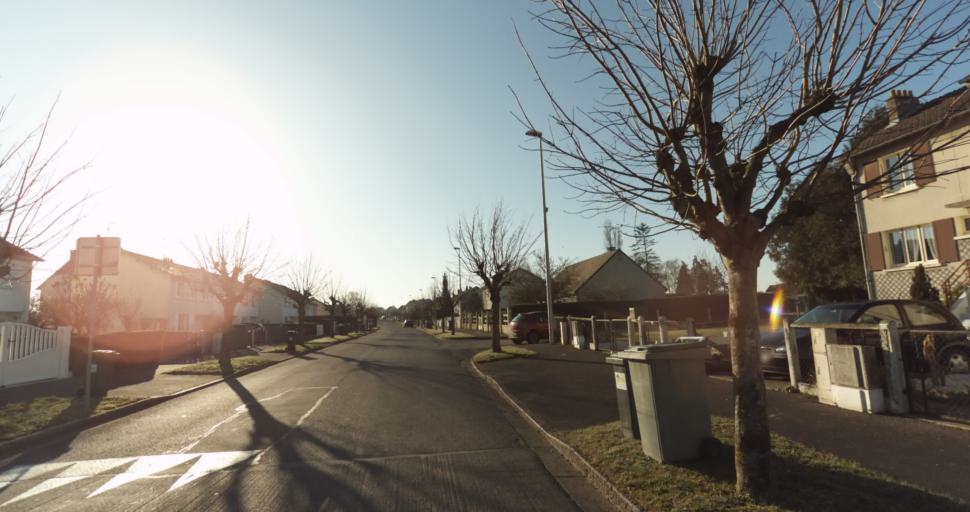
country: FR
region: Lower Normandy
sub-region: Departement du Calvados
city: Saint-Pierre-sur-Dives
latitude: 49.0126
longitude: -0.0378
